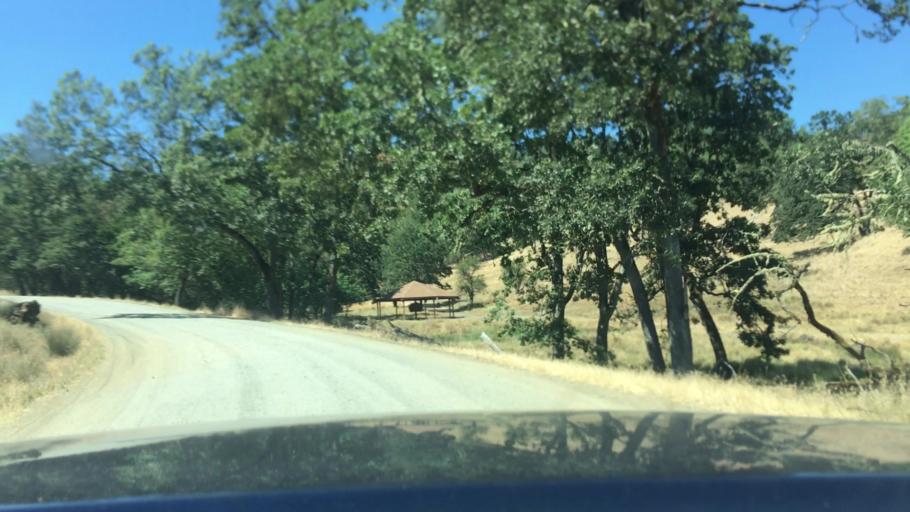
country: US
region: Oregon
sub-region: Douglas County
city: Winston
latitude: 43.1333
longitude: -123.4372
